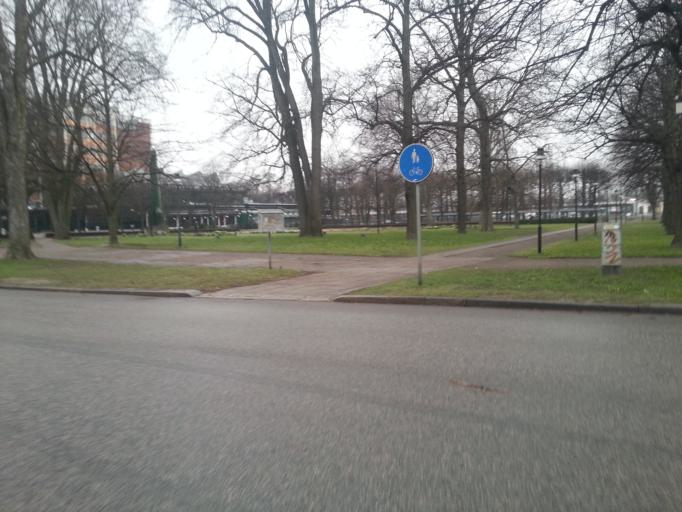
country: SE
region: OEstergoetland
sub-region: Norrkopings Kommun
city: Norrkoping
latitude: 58.5947
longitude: 16.1837
